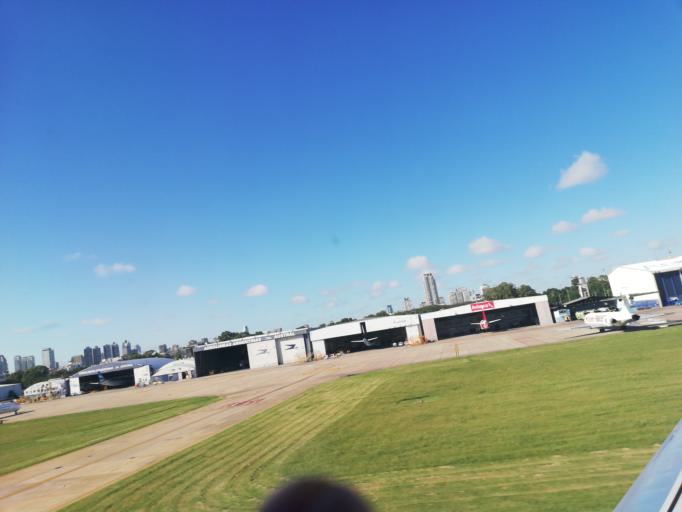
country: AR
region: Buenos Aires F.D.
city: Retiro
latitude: -34.5618
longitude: -58.4112
